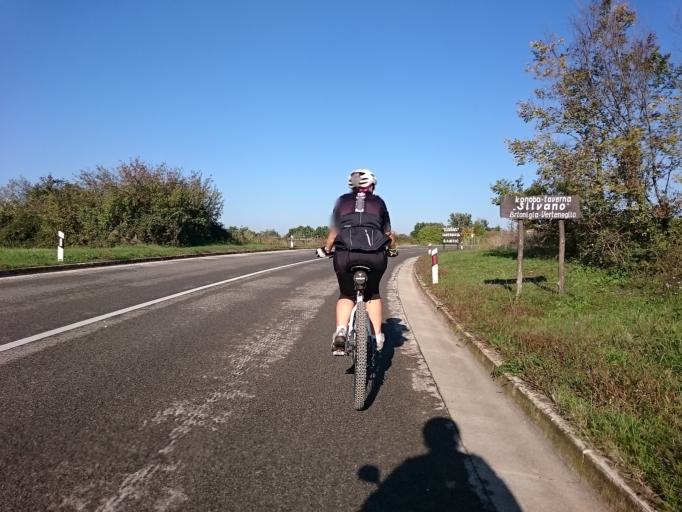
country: HR
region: Istarska
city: Buje
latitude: 45.3752
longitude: 13.6223
